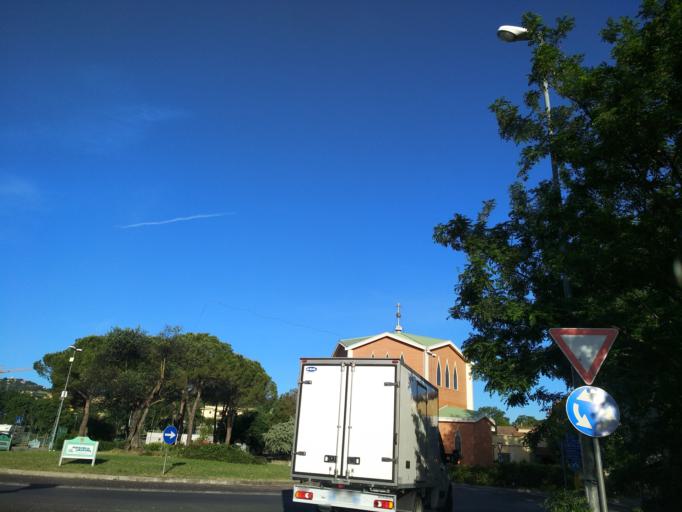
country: IT
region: The Marches
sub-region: Provincia di Pesaro e Urbino
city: Cappone
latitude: 43.8341
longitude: 12.7464
